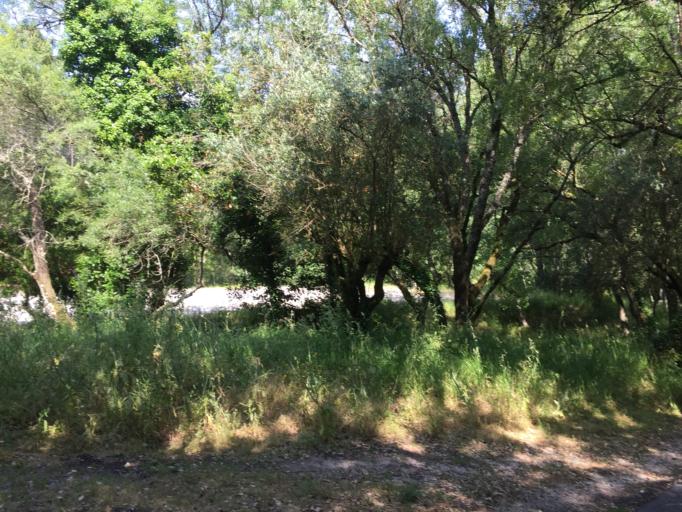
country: PT
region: Lisbon
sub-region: Mafra
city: Milharado
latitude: 38.9027
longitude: -9.1858
